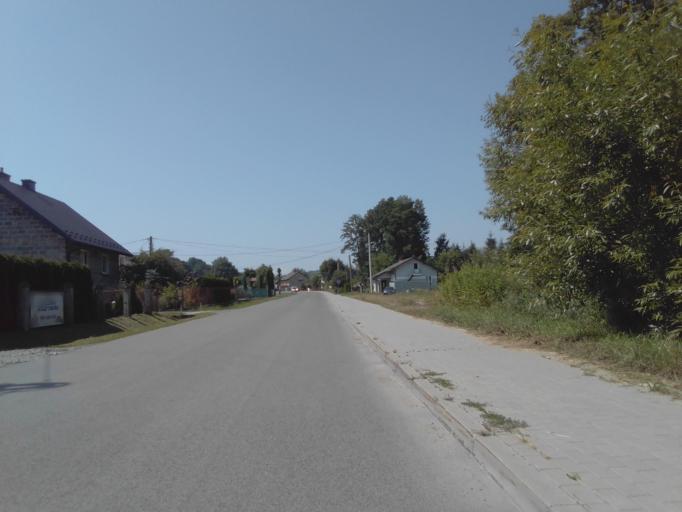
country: PL
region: Subcarpathian Voivodeship
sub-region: Powiat ropczycko-sedziszowski
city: Zagorzyce
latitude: 50.0498
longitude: 21.6651
